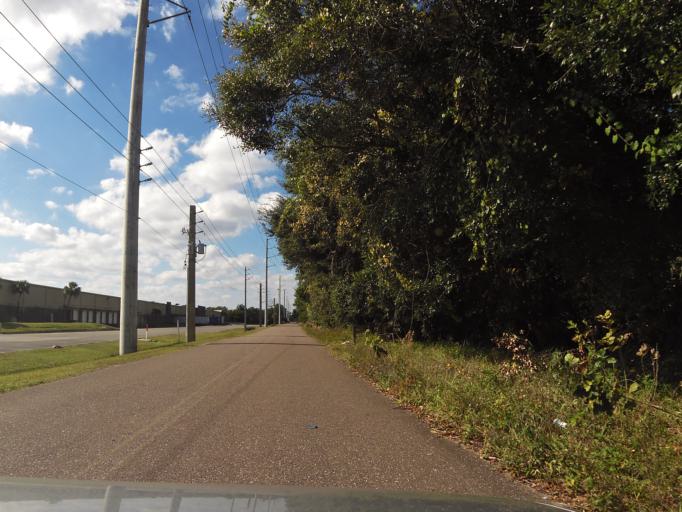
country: US
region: Florida
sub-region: Duval County
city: Jacksonville
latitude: 30.4102
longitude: -81.6369
